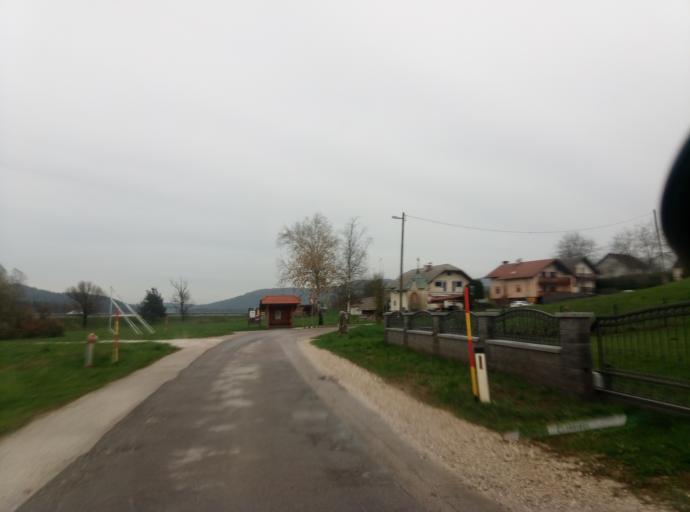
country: SI
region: Vodice
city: Vodice
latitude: 46.1771
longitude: 14.4839
